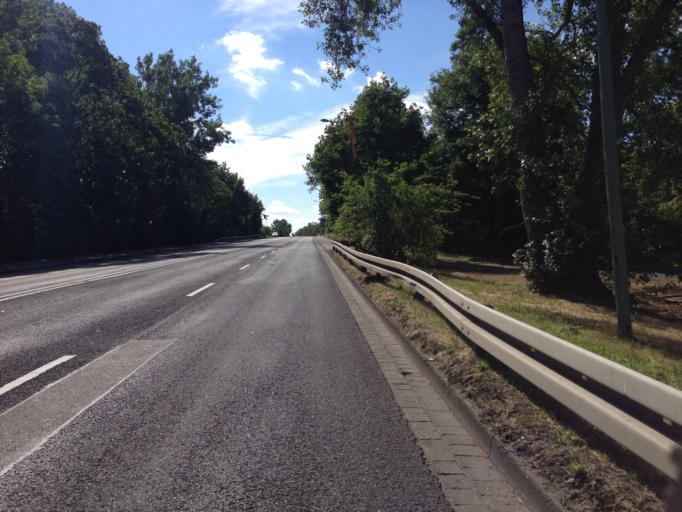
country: DE
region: Hesse
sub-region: Regierungsbezirk Darmstadt
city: Hanau am Main
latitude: 50.1233
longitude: 8.9515
